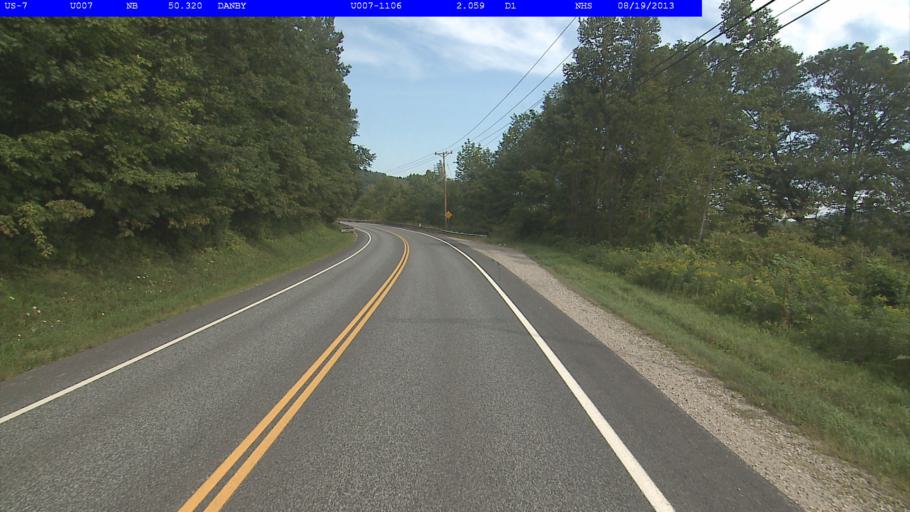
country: US
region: Vermont
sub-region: Rutland County
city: West Rutland
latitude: 43.3917
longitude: -72.9973
